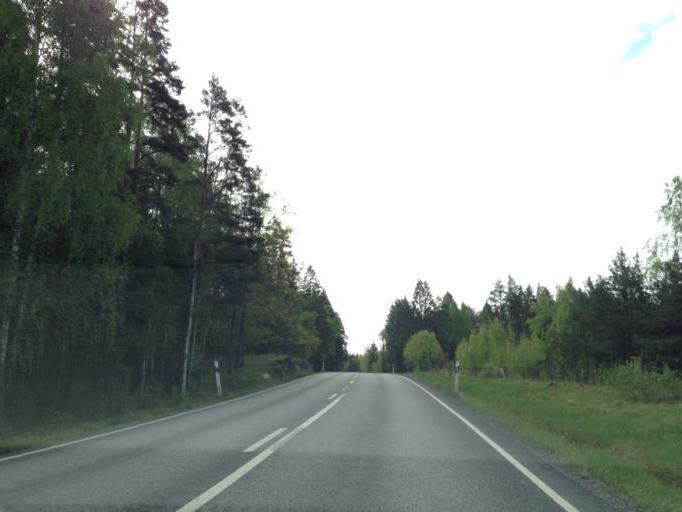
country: SE
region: Soedermanland
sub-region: Flens Kommun
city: Malmkoping
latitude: 59.0571
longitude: 16.8255
